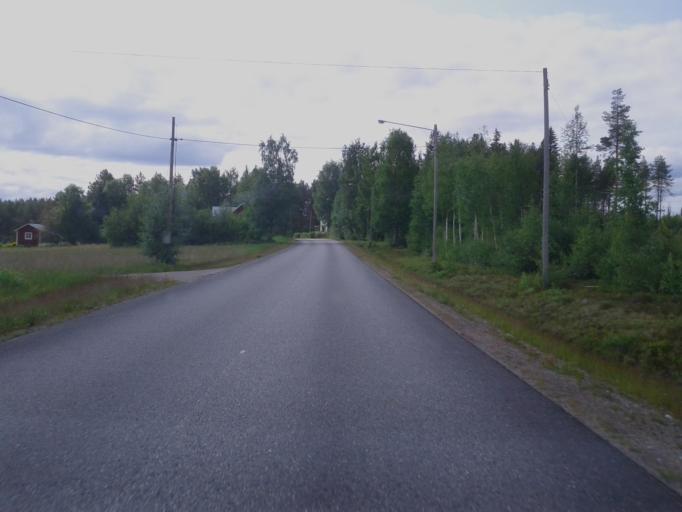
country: SE
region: Vaesterbotten
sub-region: Sorsele Kommun
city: Sorsele
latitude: 65.2794
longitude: 17.9336
